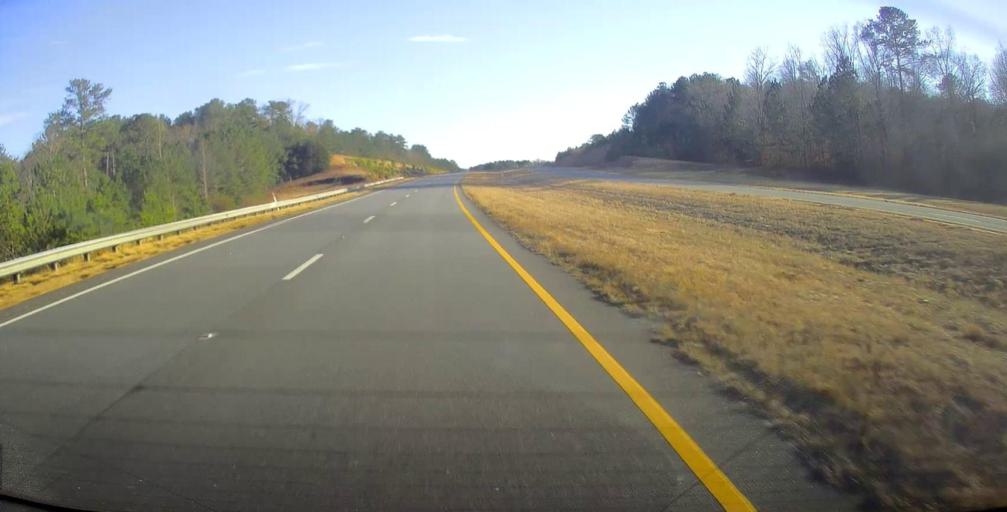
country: US
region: Georgia
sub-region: Upson County
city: Thomaston
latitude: 32.8363
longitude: -84.3094
